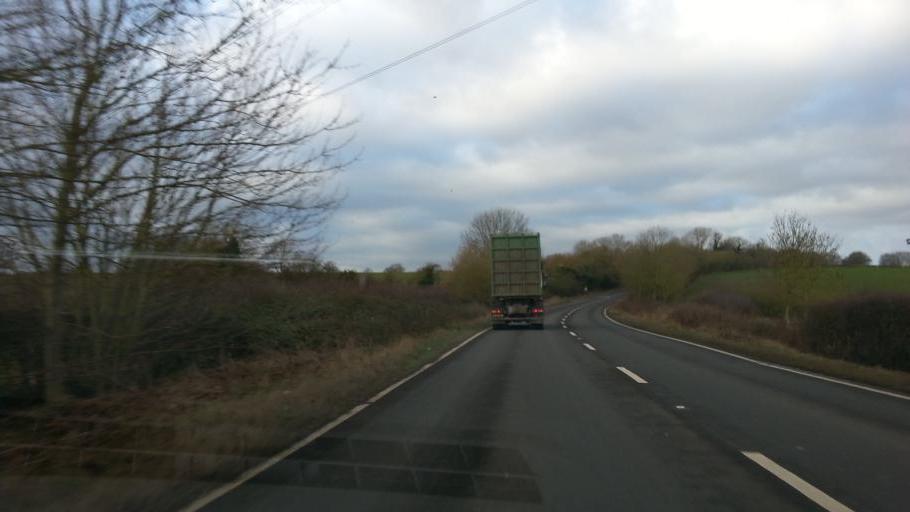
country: GB
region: England
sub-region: Nottinghamshire
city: Newark on Trent
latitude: 53.1063
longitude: -0.8466
